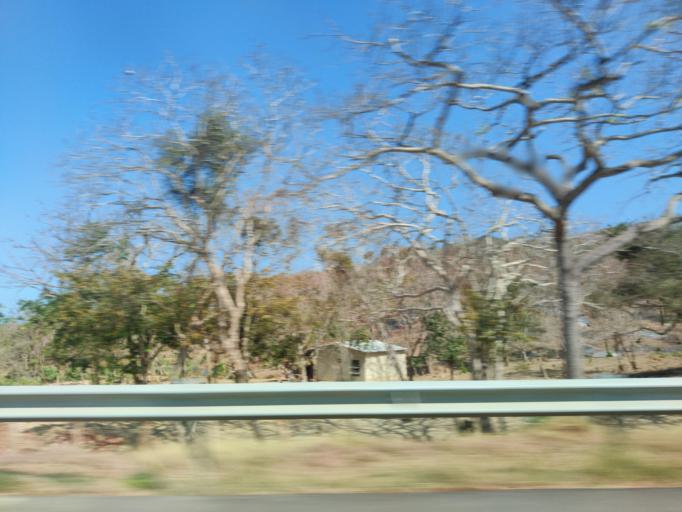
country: CO
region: Atlantico
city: Tubara
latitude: 10.9426
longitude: -75.0180
